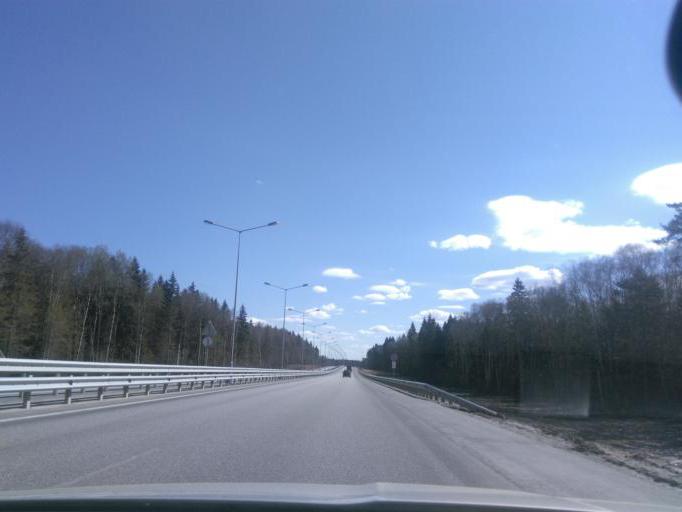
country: RU
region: Moskovskaya
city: Rzhavki
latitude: 56.0040
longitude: 37.2644
